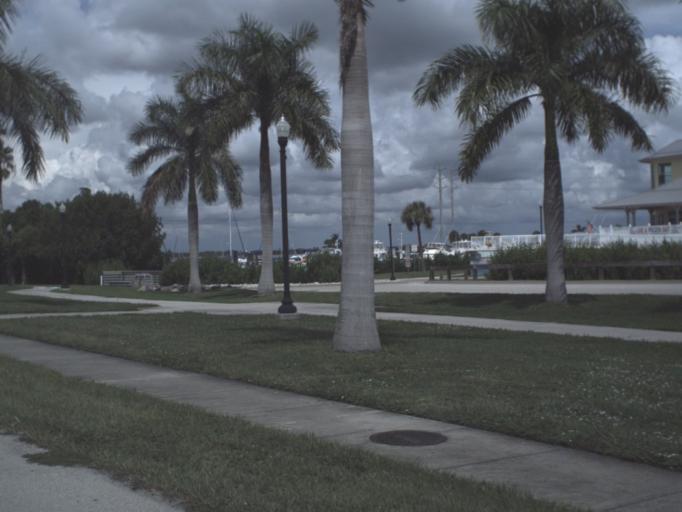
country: US
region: Florida
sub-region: Charlotte County
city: Punta Gorda
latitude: 26.9379
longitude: -82.0517
